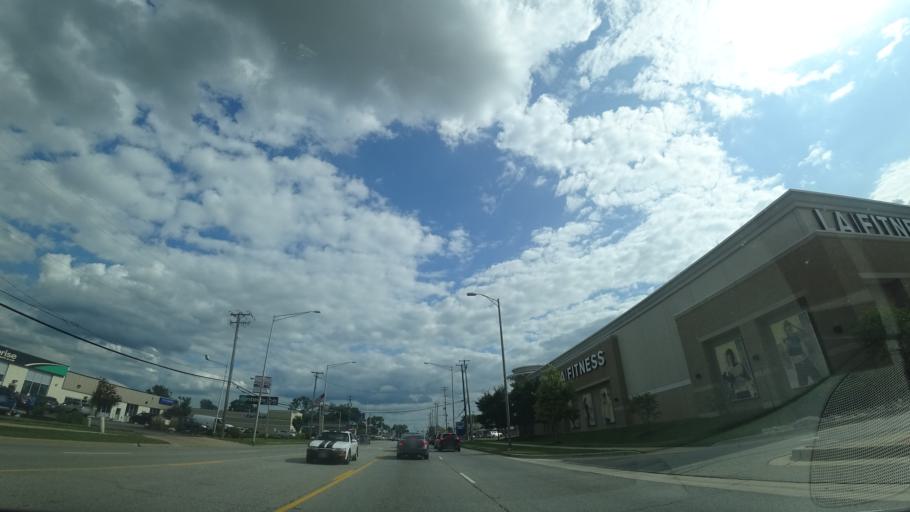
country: US
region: Illinois
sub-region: Cook County
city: Alsip
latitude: 41.6736
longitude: -87.7391
